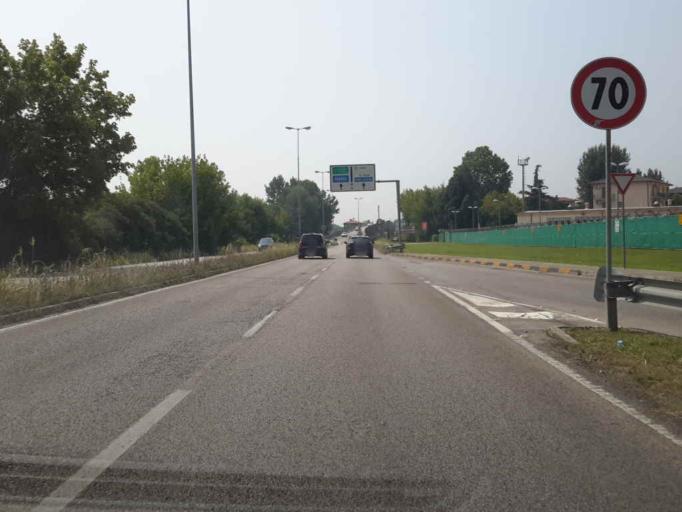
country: IT
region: Veneto
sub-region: Provincia di Vicenza
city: Villaggio Montegrappa
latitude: 45.5444
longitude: 11.5857
